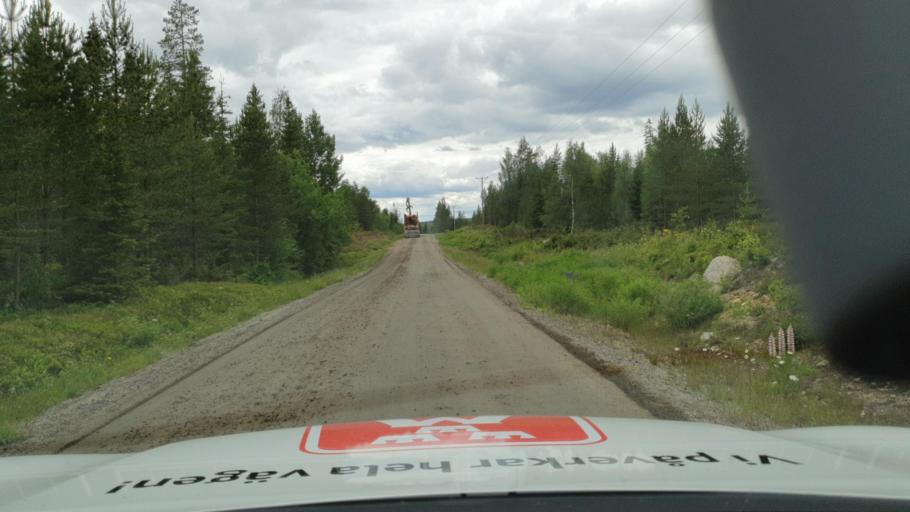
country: SE
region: Vaesterbotten
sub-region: Bjurholms Kommun
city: Bjurholm
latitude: 63.8096
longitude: 19.0622
